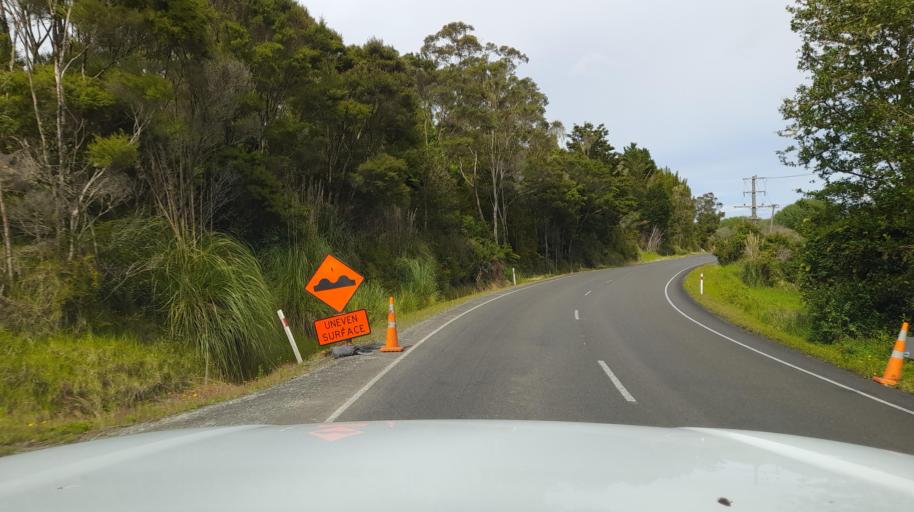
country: NZ
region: Northland
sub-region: Far North District
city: Taipa
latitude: -35.2670
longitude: 173.4993
